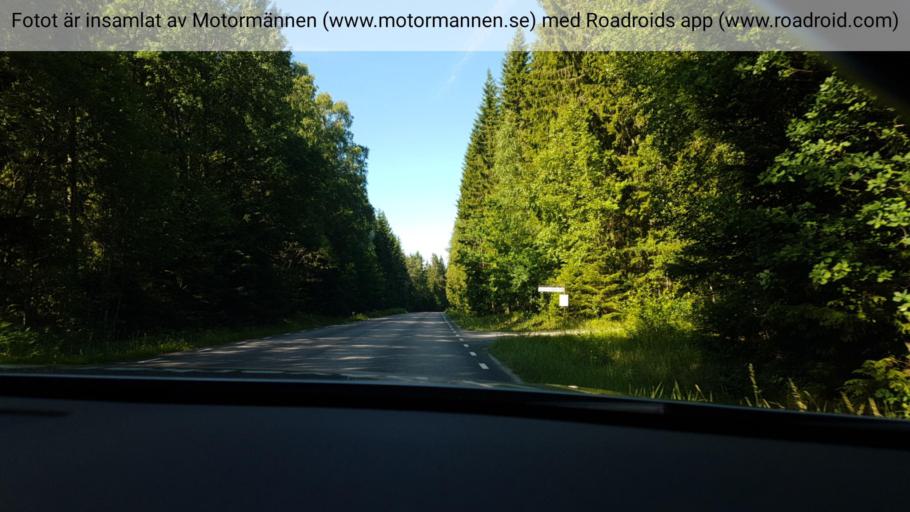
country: SE
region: Vaestra Goetaland
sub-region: Ulricehamns Kommun
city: Ulricehamn
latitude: 57.8322
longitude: 13.3141
